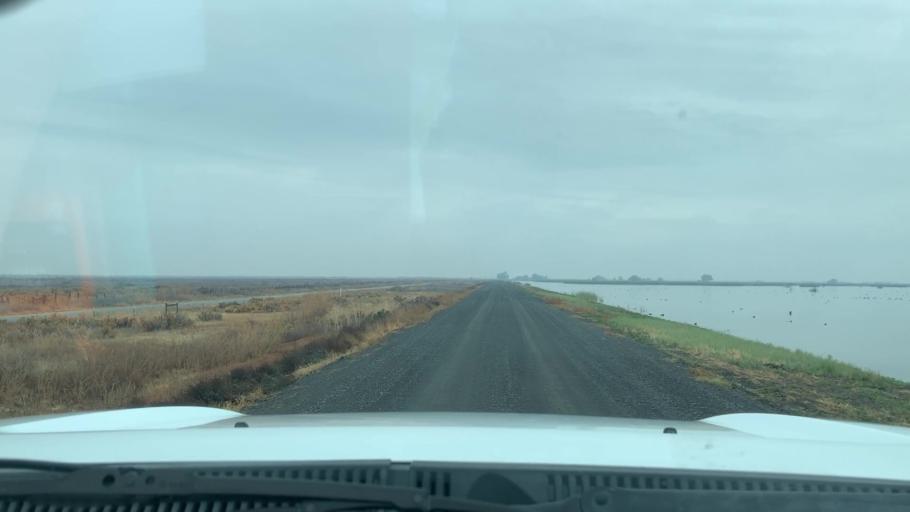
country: US
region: California
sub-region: Tulare County
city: Alpaugh
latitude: 35.7469
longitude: -119.5799
